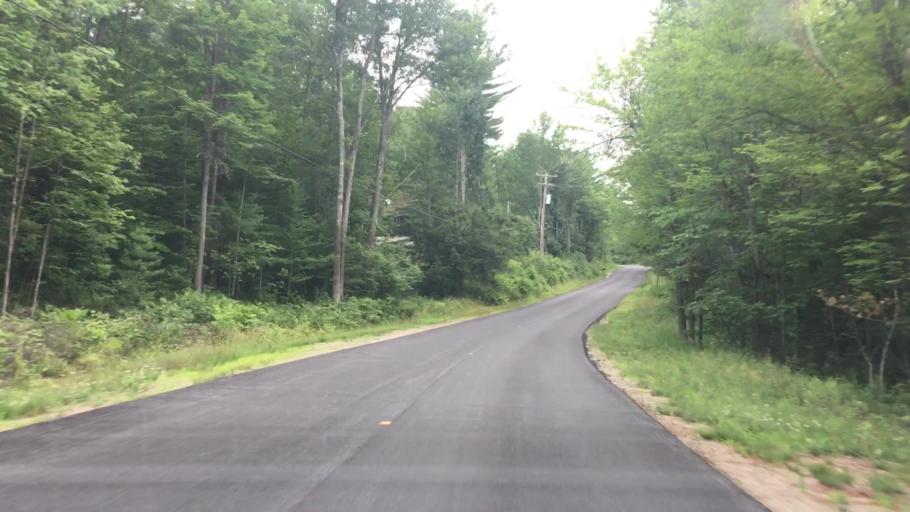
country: US
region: New York
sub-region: Essex County
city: Keeseville
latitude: 44.4247
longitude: -73.6335
